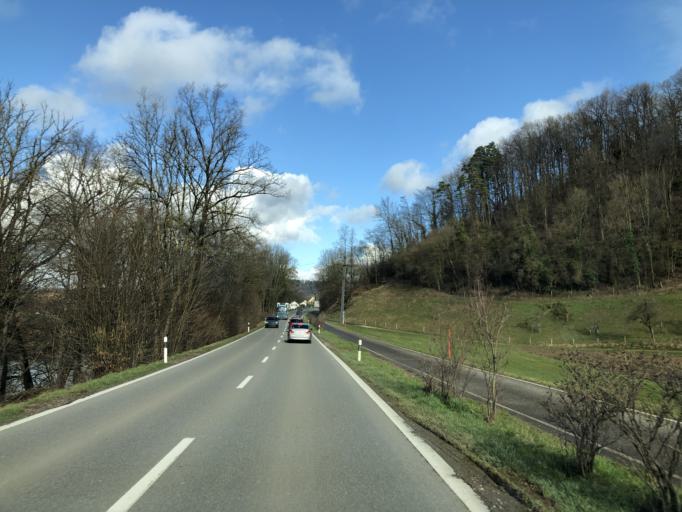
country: CH
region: Aargau
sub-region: Bezirk Baden
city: Gebenstorf
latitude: 47.4719
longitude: 8.2342
